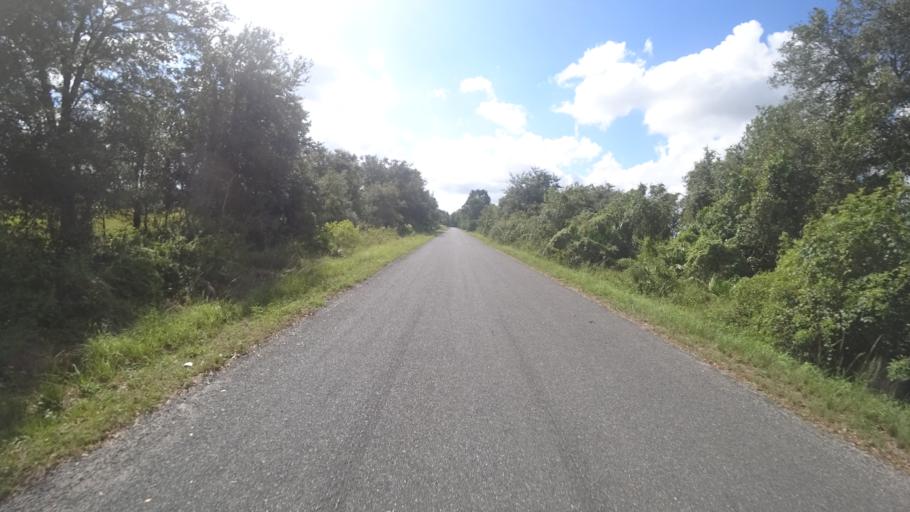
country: US
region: Florida
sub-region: Hillsborough County
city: Wimauma
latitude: 27.4632
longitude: -82.1701
